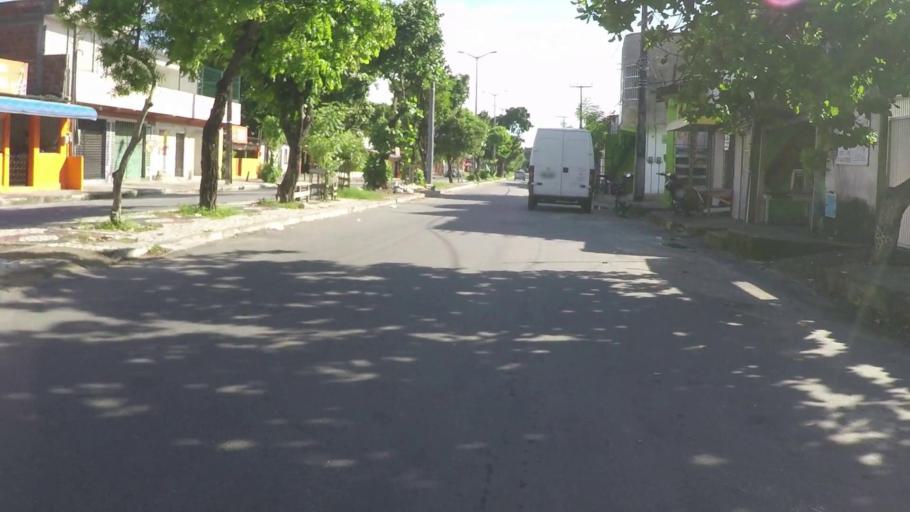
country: BR
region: Ceara
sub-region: Fortaleza
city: Fortaleza
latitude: -3.6985
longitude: -38.5870
